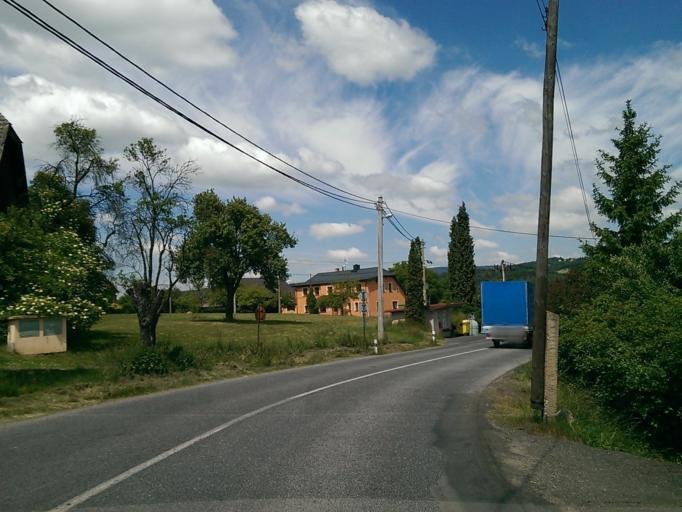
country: CZ
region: Liberecky
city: Zelezny Brod
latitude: 50.6346
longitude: 15.2773
